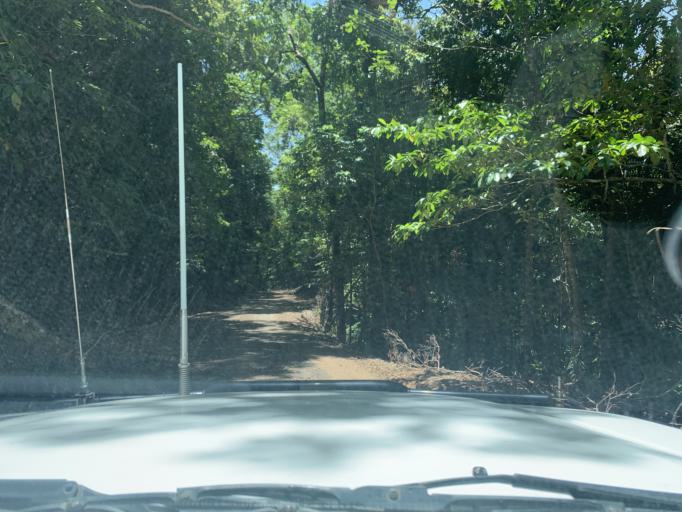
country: AU
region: Queensland
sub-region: Cairns
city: Redlynch
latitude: -16.9623
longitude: 145.6462
